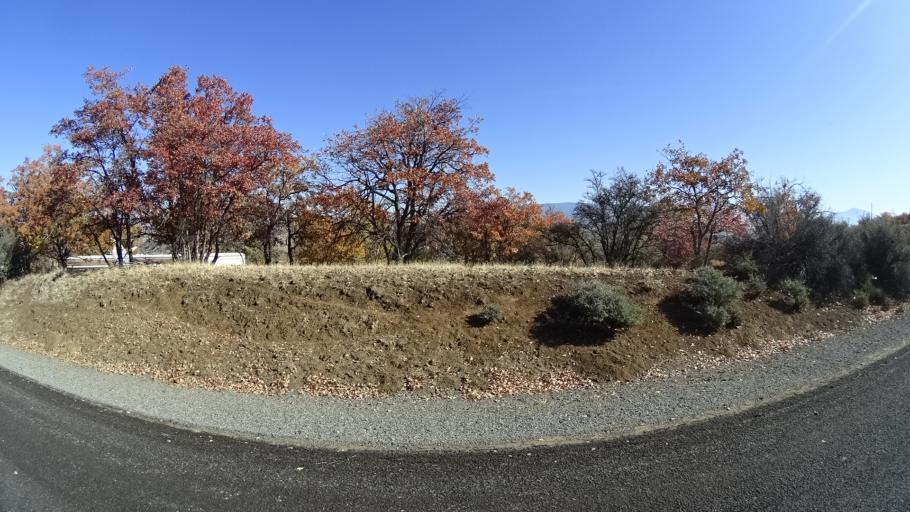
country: US
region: California
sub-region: Siskiyou County
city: Montague
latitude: 41.8784
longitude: -122.4926
